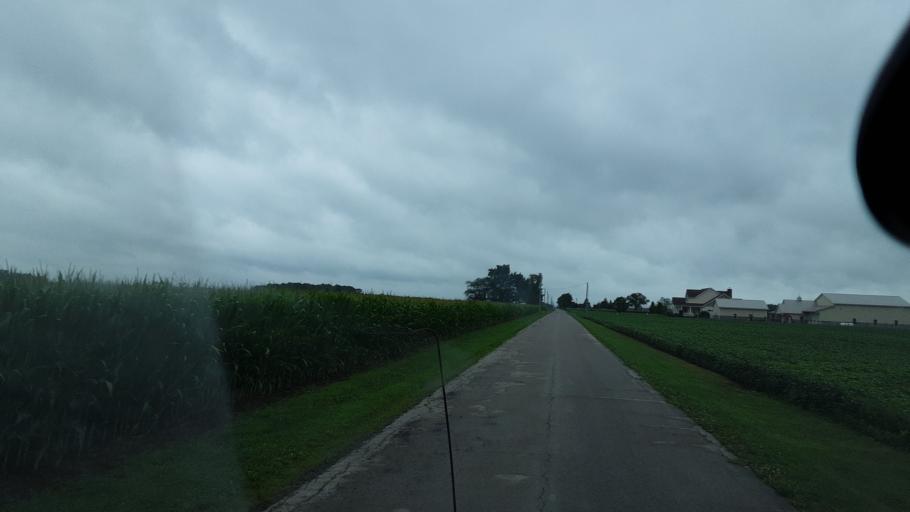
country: US
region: Ohio
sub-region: Van Wert County
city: Convoy
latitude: 40.8296
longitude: -84.7507
